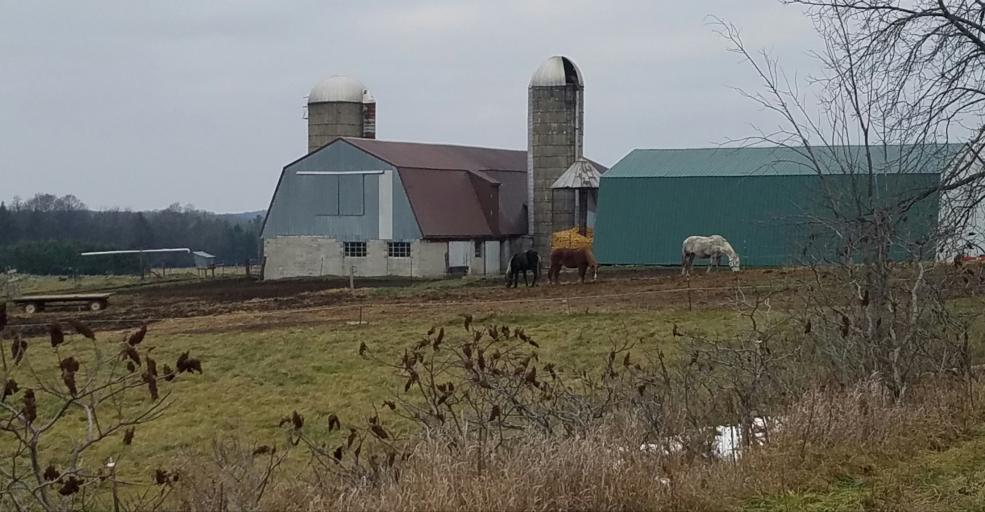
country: US
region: Michigan
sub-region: Wexford County
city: Manton
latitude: 44.4006
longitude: -85.4797
